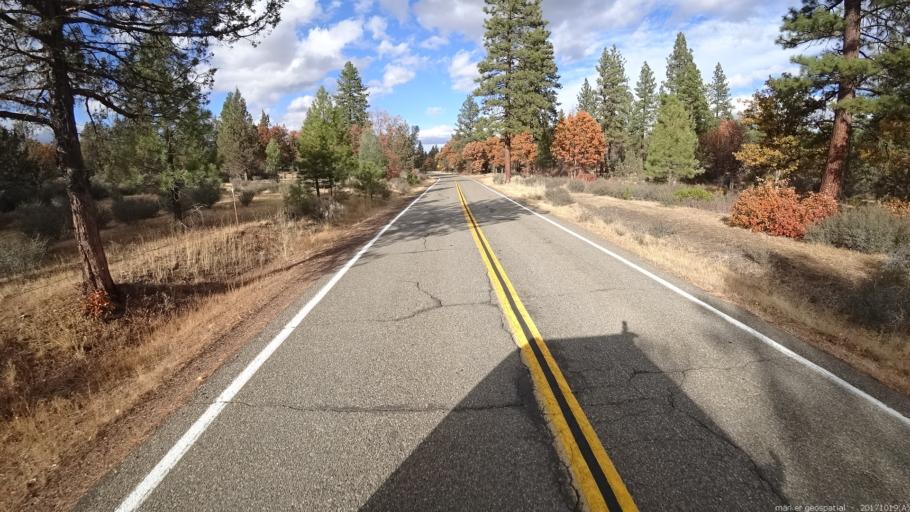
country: US
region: California
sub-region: Shasta County
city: Burney
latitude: 40.9556
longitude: -121.4404
